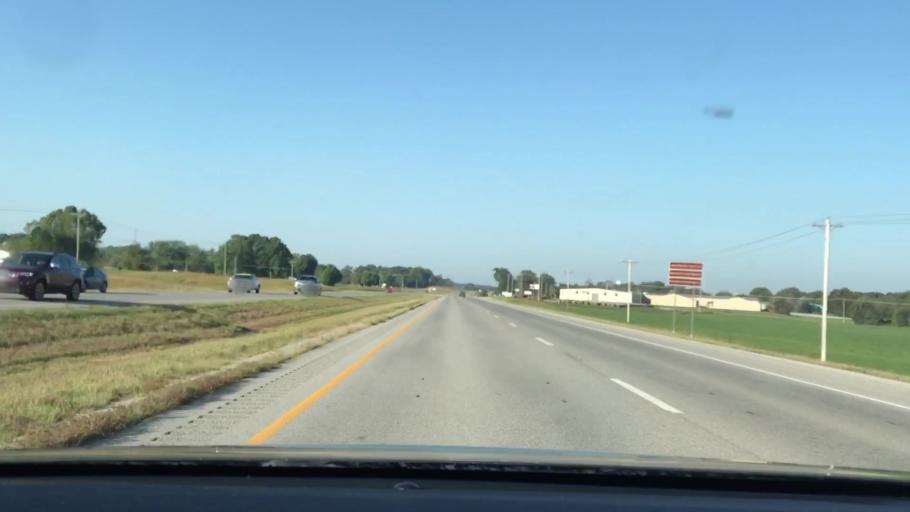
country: US
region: Kentucky
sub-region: Trigg County
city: Cadiz
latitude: 36.8742
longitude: -87.7575
